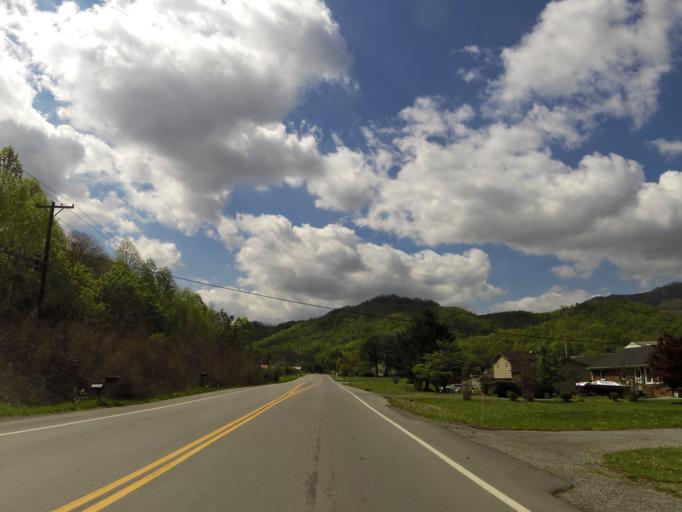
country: US
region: Kentucky
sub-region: Bell County
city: Middlesboro
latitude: 36.6113
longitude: -83.7574
